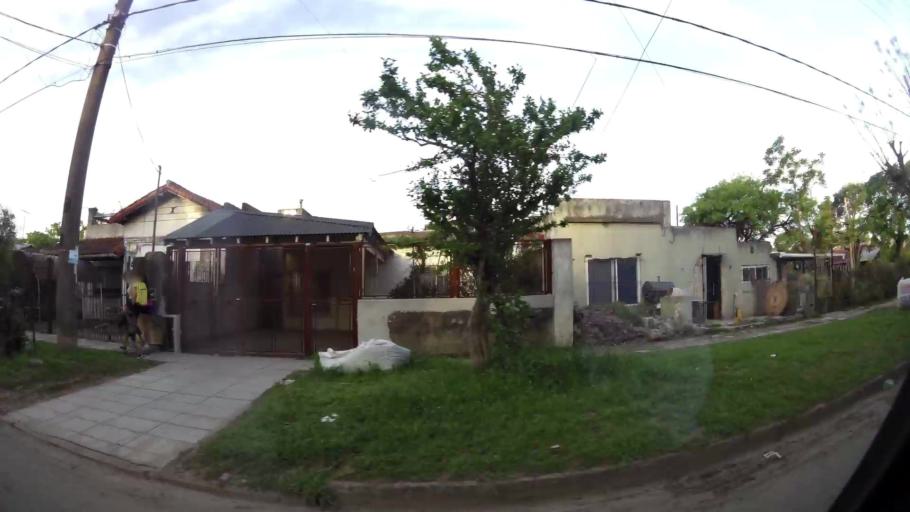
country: AR
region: Buenos Aires
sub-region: Partido de Almirante Brown
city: Adrogue
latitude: -34.7885
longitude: -58.3467
